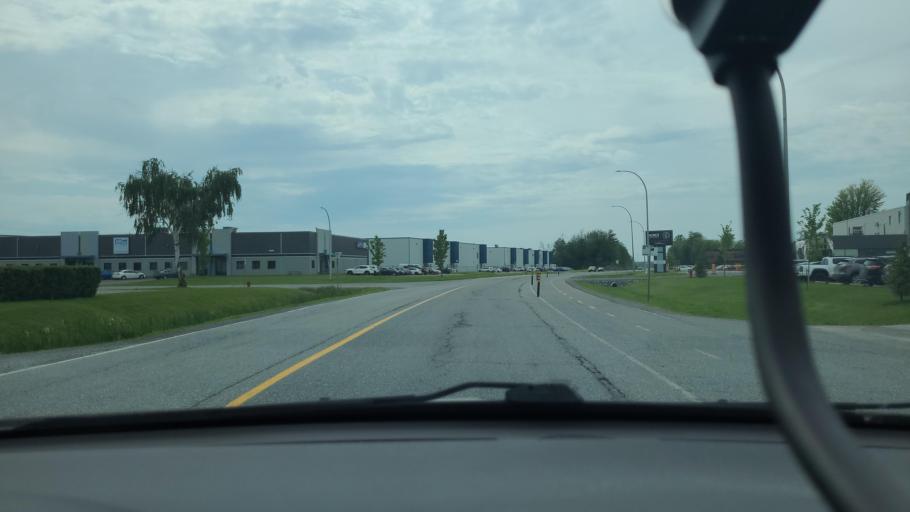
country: CA
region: Quebec
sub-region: Monteregie
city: Saint-Hyacinthe
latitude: 45.6293
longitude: -72.9892
